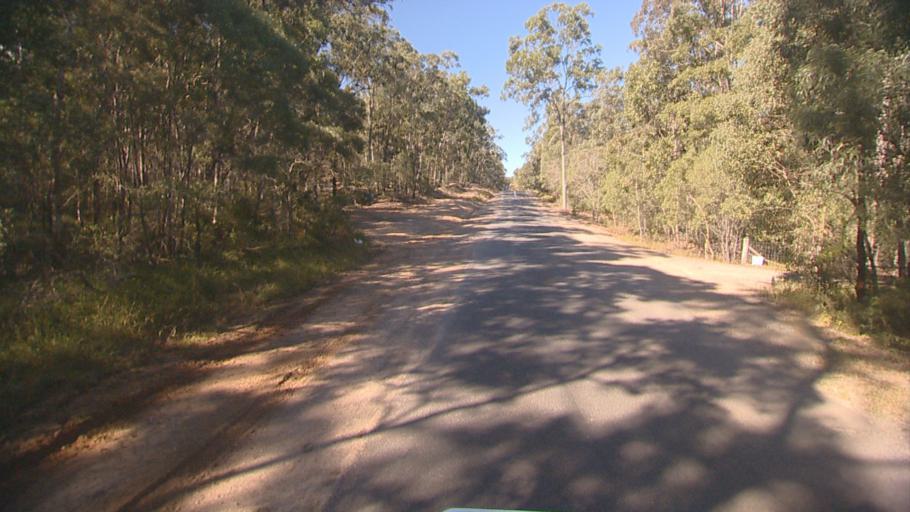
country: AU
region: Queensland
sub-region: Logan
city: Windaroo
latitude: -27.7531
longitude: 153.1499
